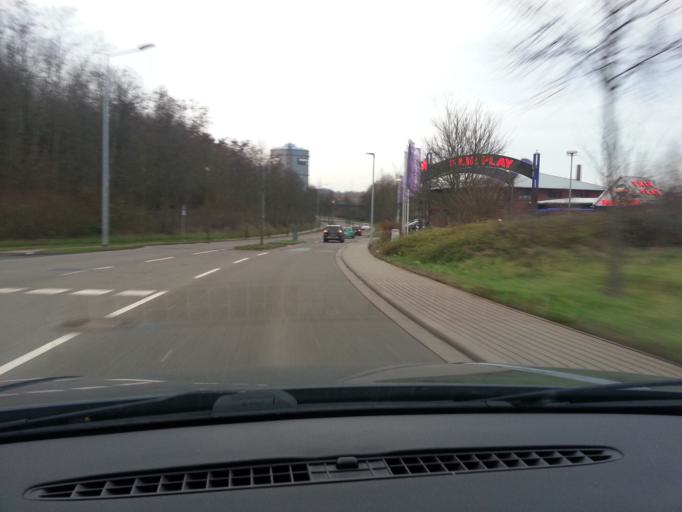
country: DE
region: Saarland
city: Neunkirchen
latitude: 49.3411
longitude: 7.1717
